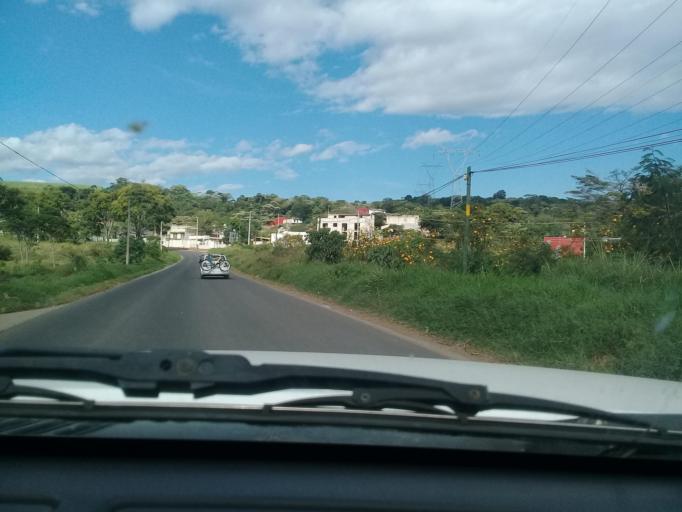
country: MX
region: Veracruz
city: El Castillo
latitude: 19.5480
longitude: -96.8774
